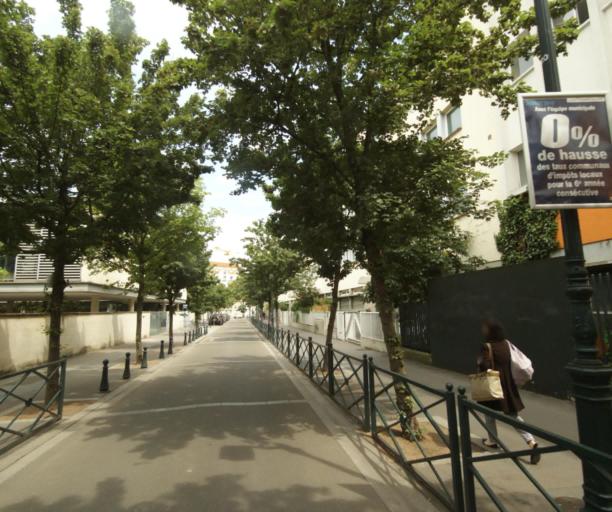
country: FR
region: Ile-de-France
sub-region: Departement des Hauts-de-Seine
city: Asnieres-sur-Seine
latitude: 48.9150
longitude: 2.2908
